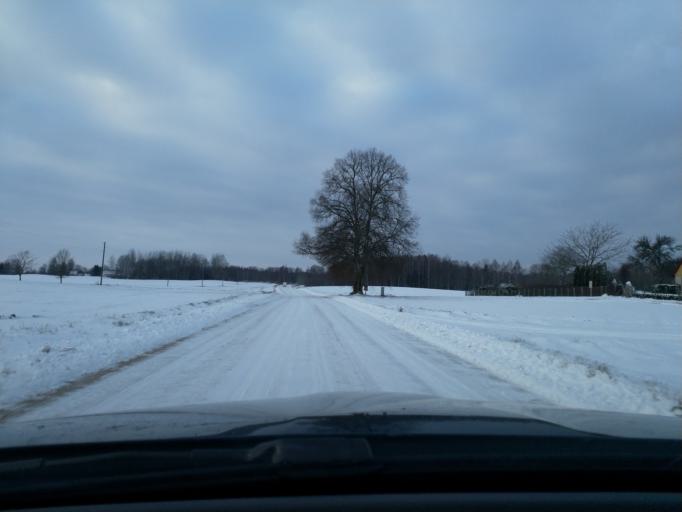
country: LV
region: Kuldigas Rajons
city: Kuldiga
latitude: 56.8695
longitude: 21.8676
